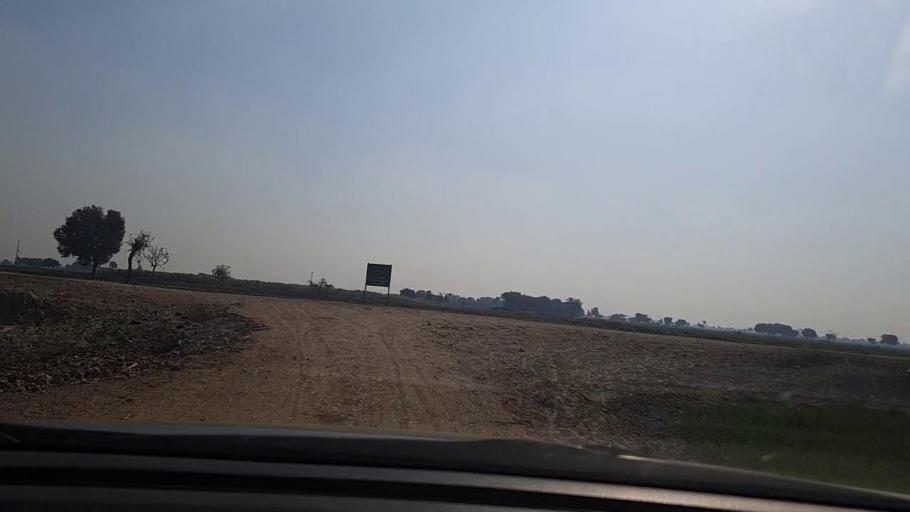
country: PK
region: Sindh
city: Sann
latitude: 26.2630
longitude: 68.0741
